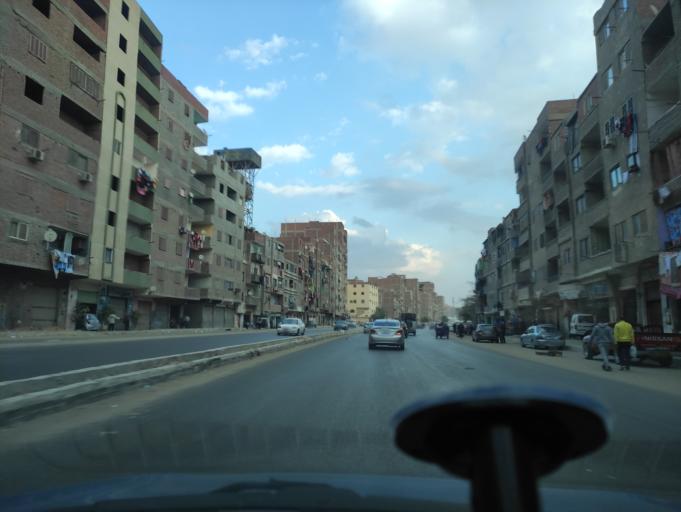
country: EG
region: Muhafazat al Qalyubiyah
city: Al Khankah
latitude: 30.1381
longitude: 31.3466
